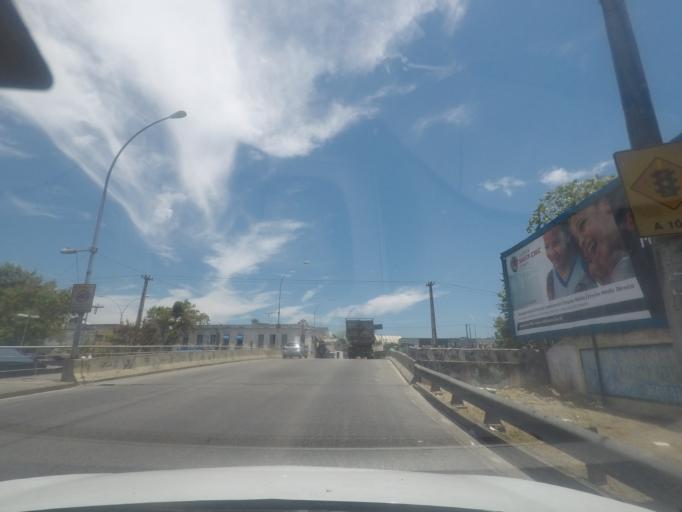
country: BR
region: Rio de Janeiro
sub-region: Itaguai
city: Itaguai
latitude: -22.9159
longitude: -43.6855
